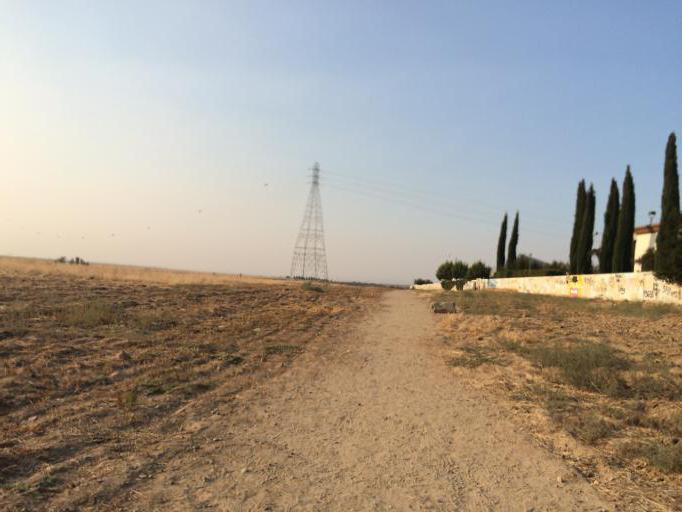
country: US
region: California
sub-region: Fresno County
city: Fresno
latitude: 36.8479
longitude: -119.8108
